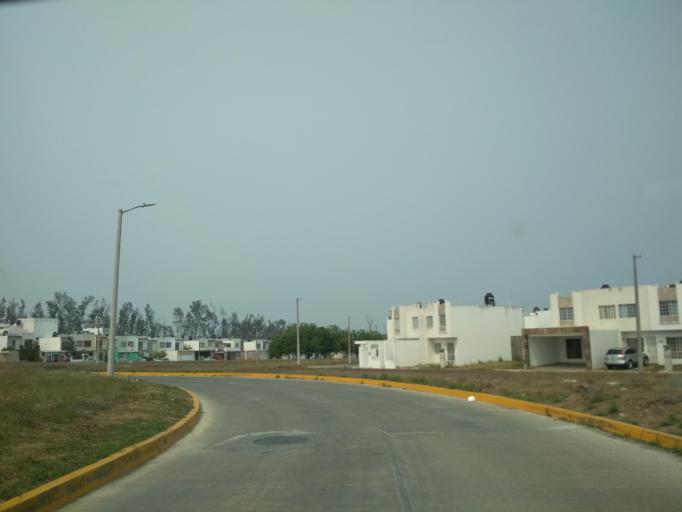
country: MX
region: Veracruz
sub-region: Veracruz
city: Las Amapolas
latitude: 19.1443
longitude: -96.2236
